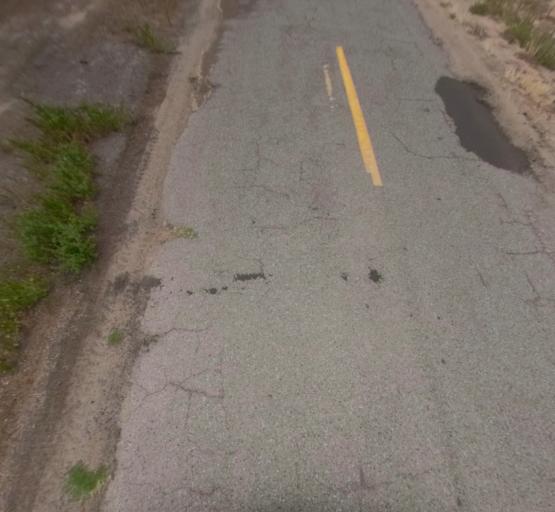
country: US
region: California
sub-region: Madera County
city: Fairmead
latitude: 37.0013
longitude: -120.2205
